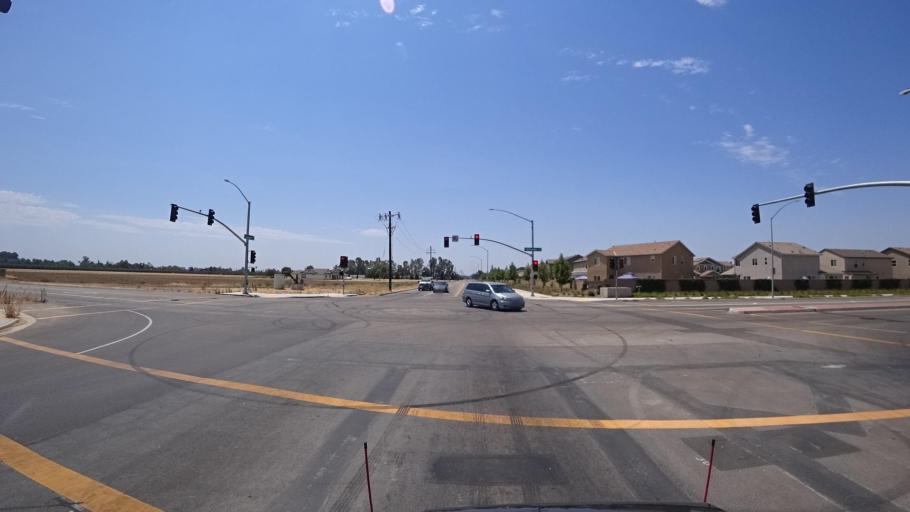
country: US
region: California
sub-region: Fresno County
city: Tarpey Village
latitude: 36.7795
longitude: -119.6551
